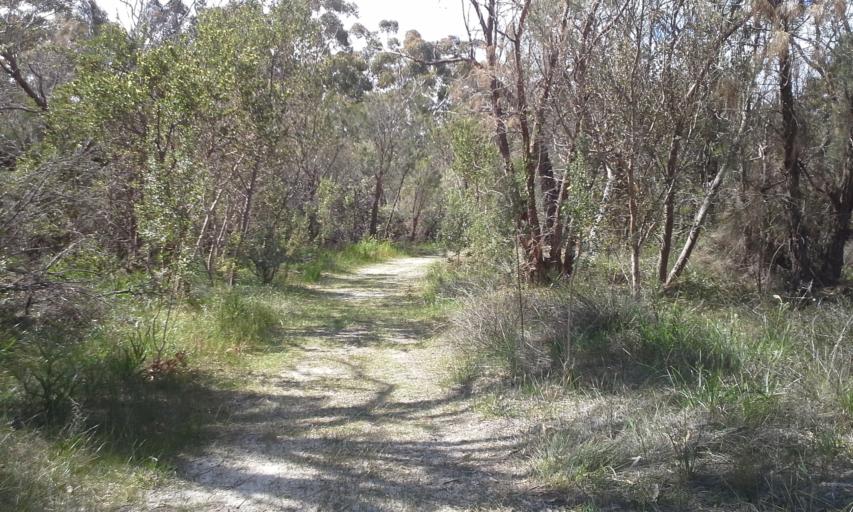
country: AU
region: Western Australia
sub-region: City of Perth
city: West Perth
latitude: -31.9617
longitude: 115.8368
